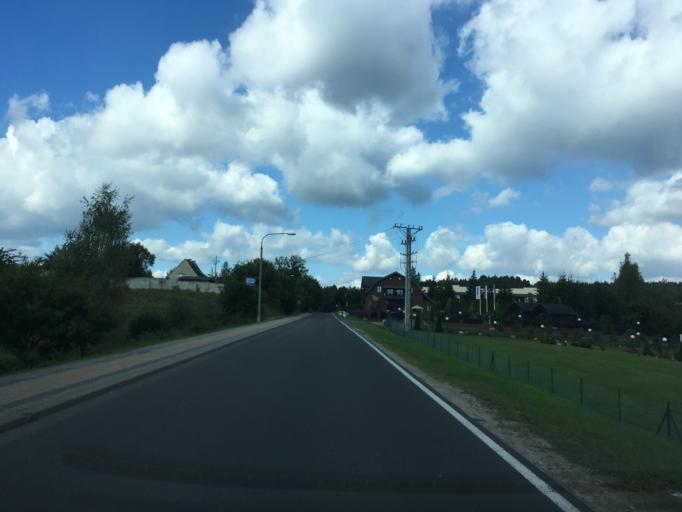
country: PL
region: Kujawsko-Pomorskie
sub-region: Powiat swiecki
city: Osie
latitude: 53.6186
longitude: 18.2689
